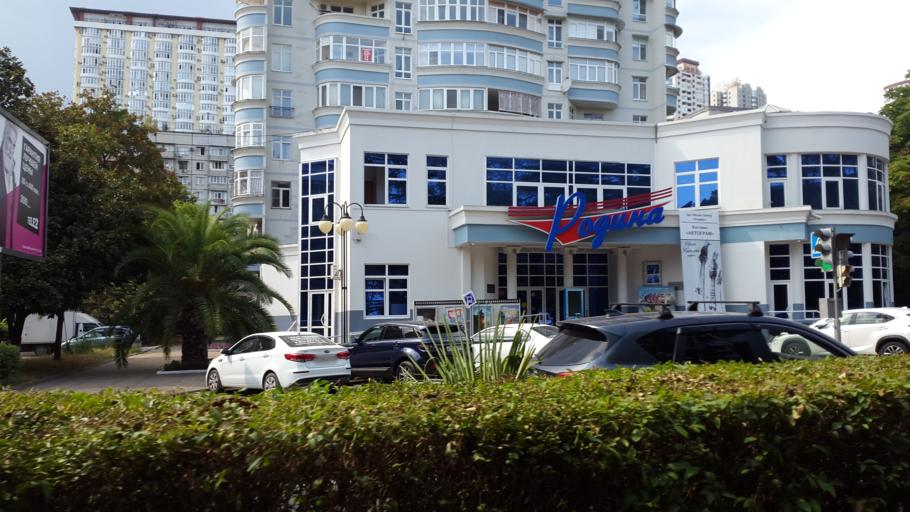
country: RU
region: Krasnodarskiy
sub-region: Sochi City
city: Sochi
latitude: 43.6002
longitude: 39.7222
